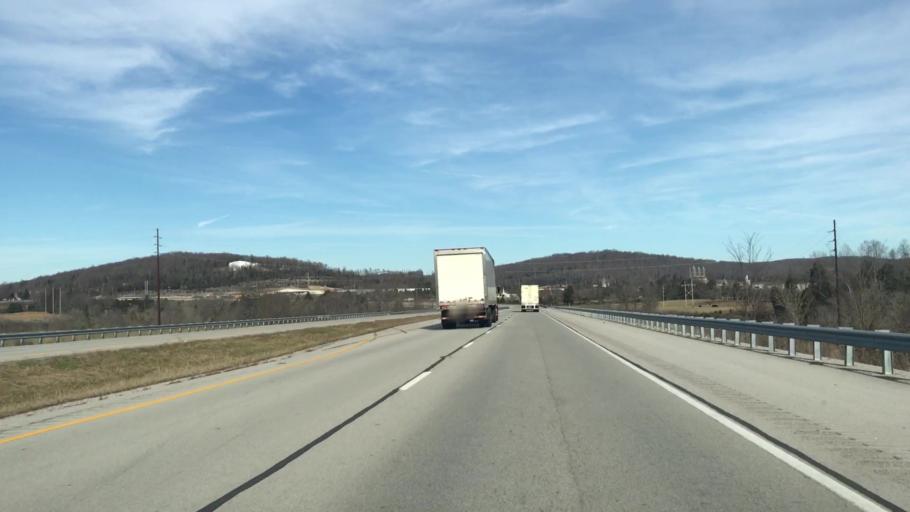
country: US
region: Kentucky
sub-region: Pulaski County
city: Somerset
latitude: 37.0404
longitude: -84.5867
